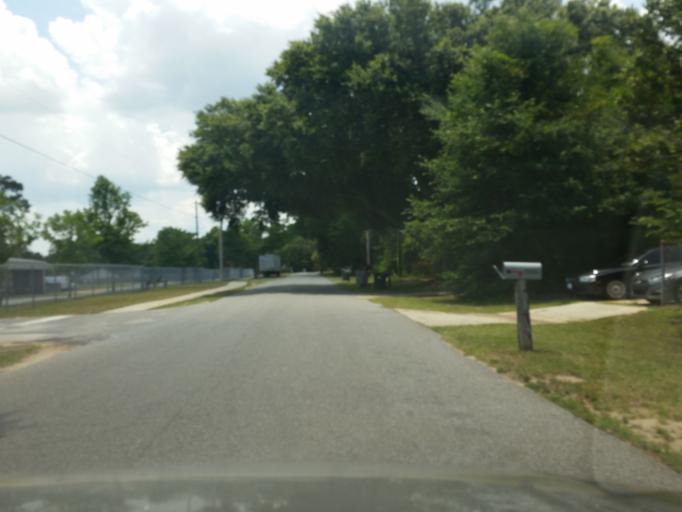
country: US
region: Florida
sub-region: Escambia County
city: Ferry Pass
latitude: 30.5144
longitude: -87.1976
